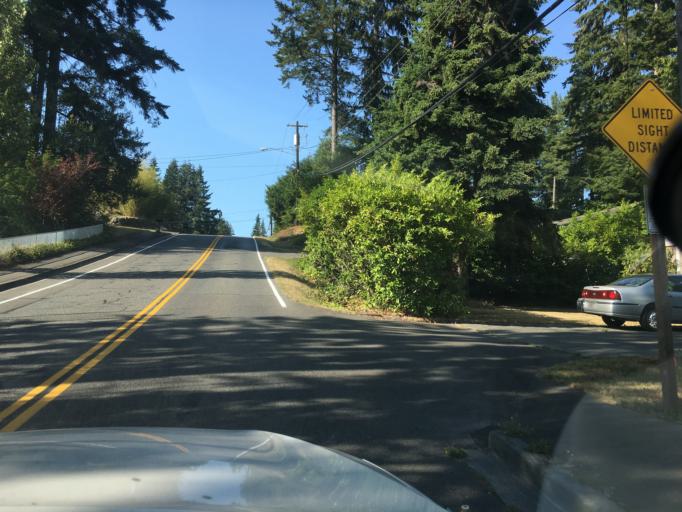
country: US
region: Washington
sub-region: Snohomish County
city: Esperance
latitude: 47.7927
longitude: -122.3596
